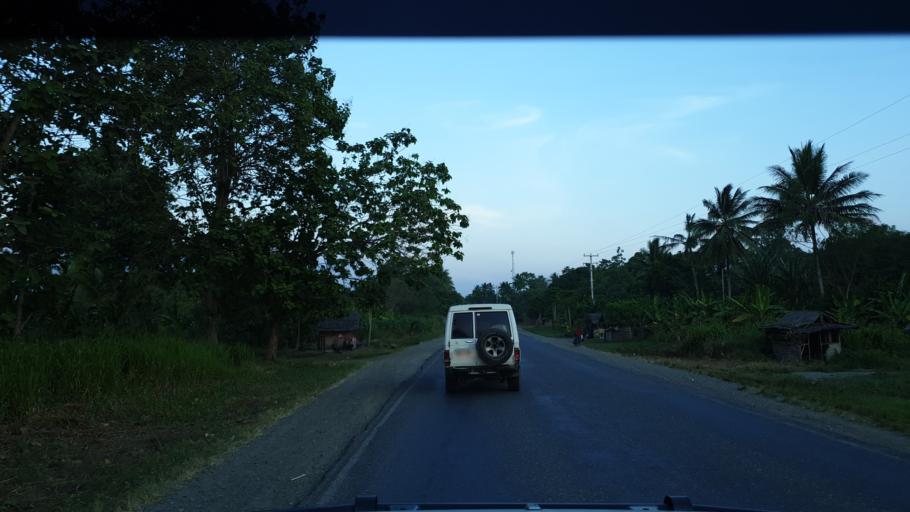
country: PG
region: Morobe
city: Lae
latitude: -6.5965
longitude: 146.7927
